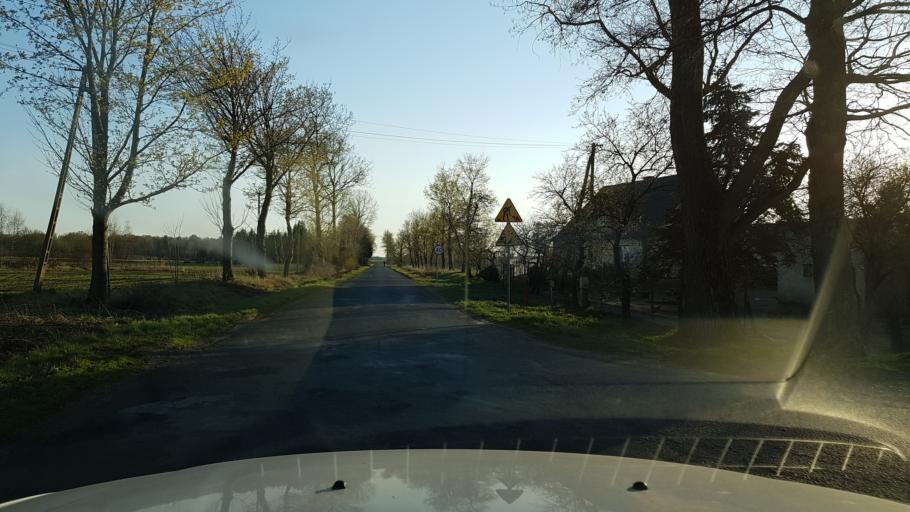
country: PL
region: West Pomeranian Voivodeship
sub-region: Powiat bialogardzki
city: Bialogard
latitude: 54.0461
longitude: 16.0055
